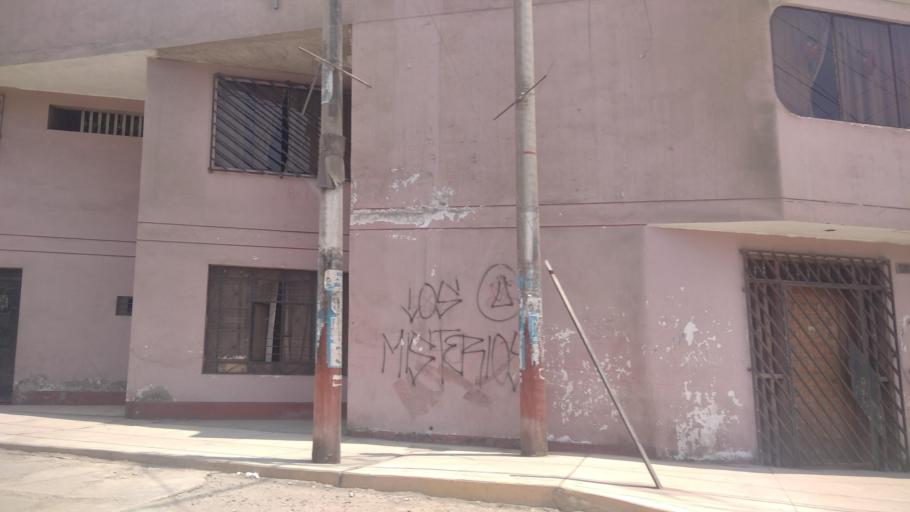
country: PE
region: Lima
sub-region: Lima
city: Independencia
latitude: -11.9685
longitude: -76.9872
